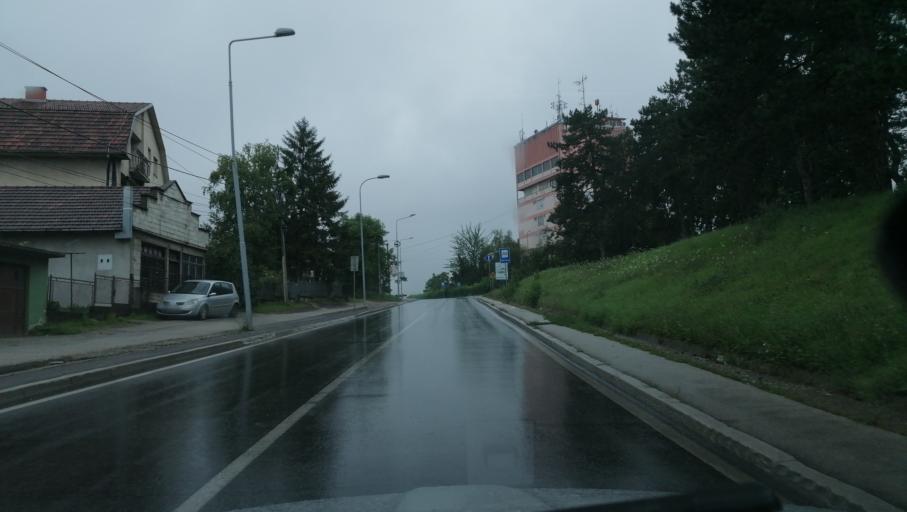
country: RS
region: Central Serbia
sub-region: Raski Okrug
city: Kraljevo
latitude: 43.7288
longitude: 20.6733
